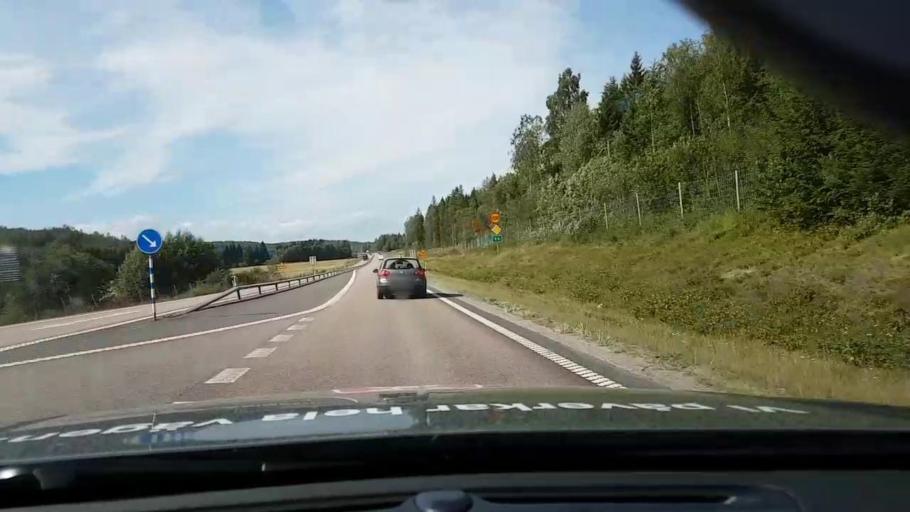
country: SE
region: Vaesternorrland
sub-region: OErnskoeldsviks Kommun
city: Ornskoldsvik
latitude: 63.2979
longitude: 18.8692
